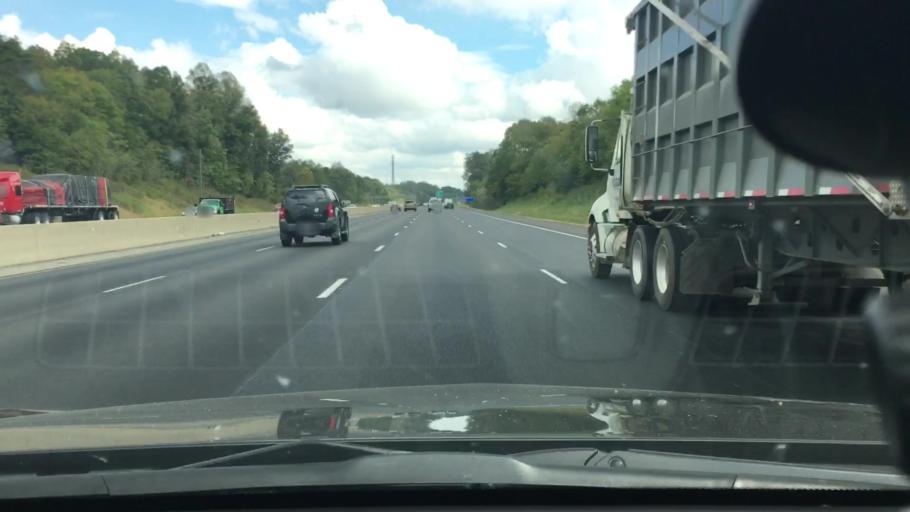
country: US
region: North Carolina
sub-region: Guilford County
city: Gibsonville
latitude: 36.0612
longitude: -79.5857
